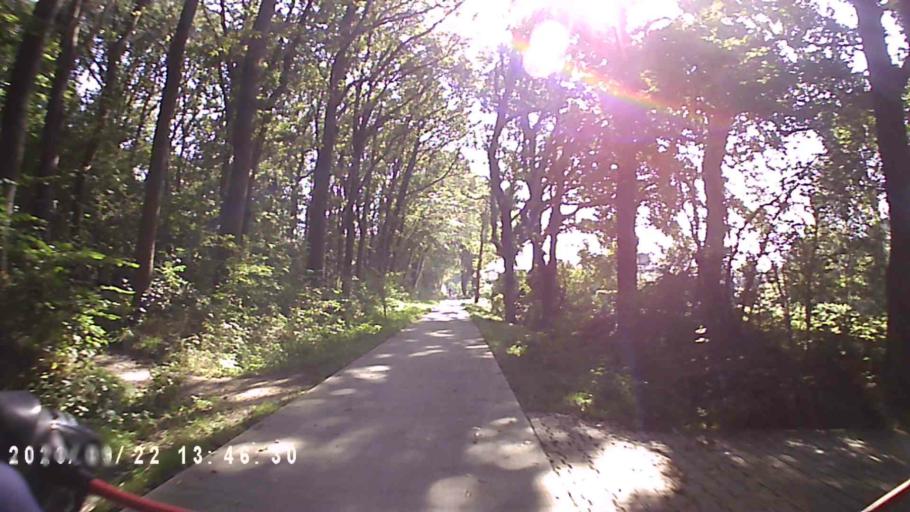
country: NL
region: Groningen
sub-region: Gemeente Leek
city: Leek
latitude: 53.1433
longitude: 6.4090
